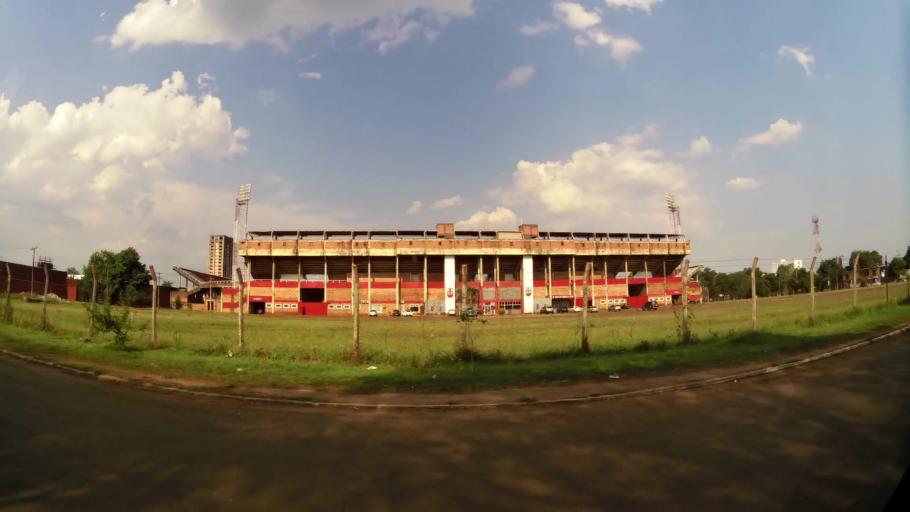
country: PY
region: Alto Parana
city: Presidente Franco
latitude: -25.5271
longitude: -54.6138
